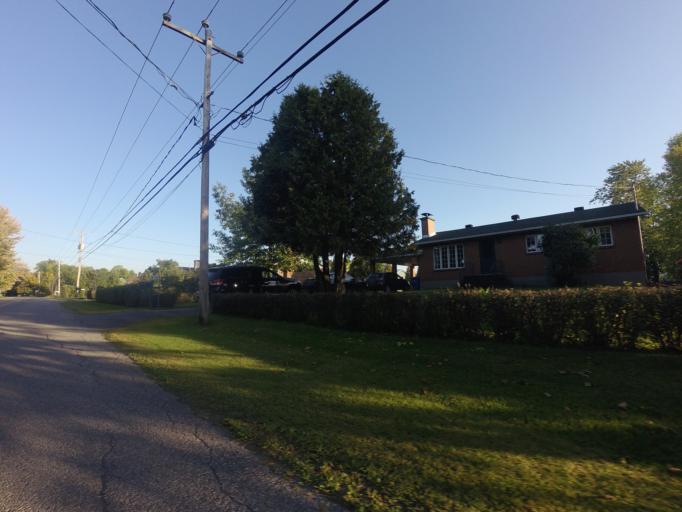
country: CA
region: Quebec
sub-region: Monteregie
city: Rigaud
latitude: 45.4791
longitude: -74.2416
